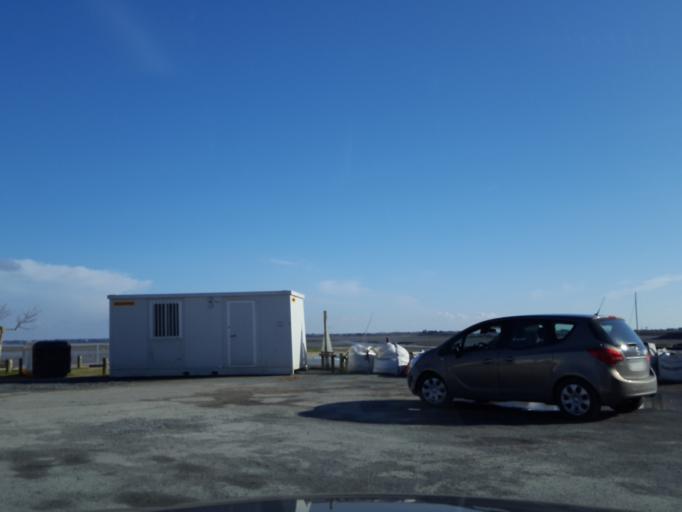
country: FR
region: Poitou-Charentes
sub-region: Departement de la Charente-Maritime
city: La Couarde-sur-Mer
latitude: 46.2163
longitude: -1.4391
